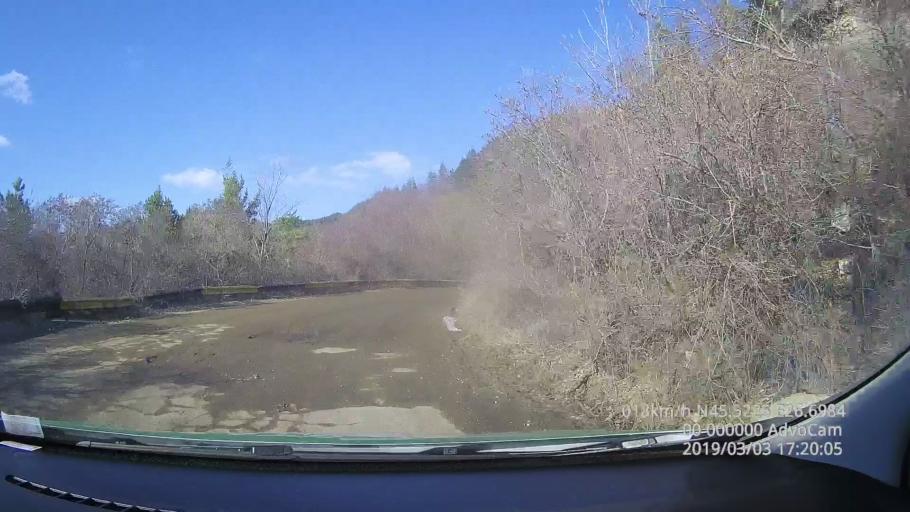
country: RO
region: Buzau
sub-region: Comuna Bisoca
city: Bisoca
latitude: 45.5226
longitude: 26.6983
